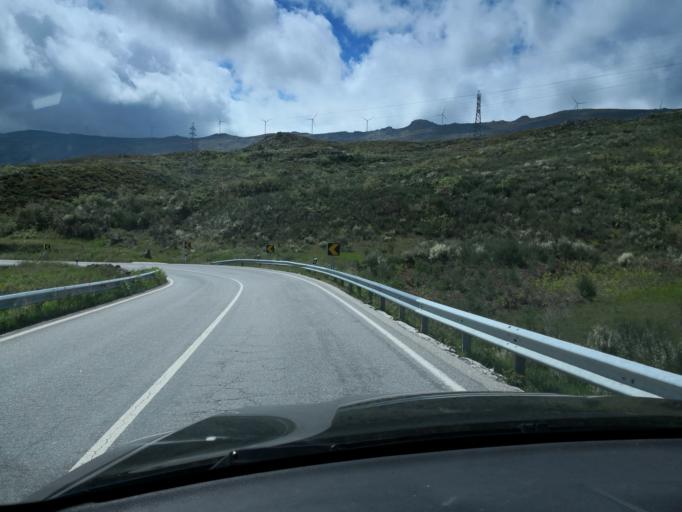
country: PT
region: Vila Real
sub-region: Vila Real
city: Vila Real
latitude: 41.3798
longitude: -7.7161
